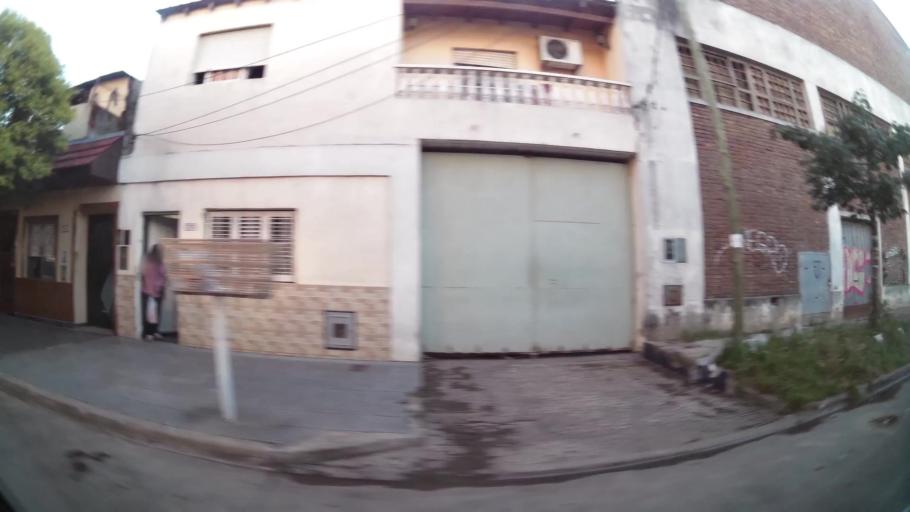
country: AR
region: Buenos Aires F.D.
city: Villa Lugano
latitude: -34.6978
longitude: -58.4863
